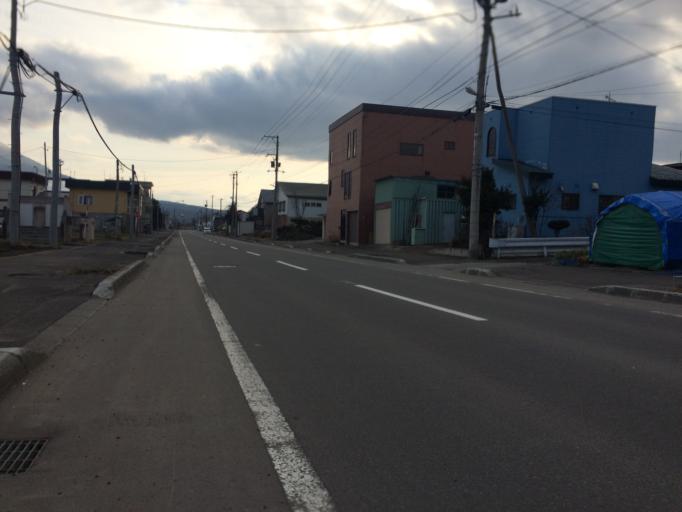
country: JP
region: Hokkaido
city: Niseko Town
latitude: 42.9028
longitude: 140.7665
